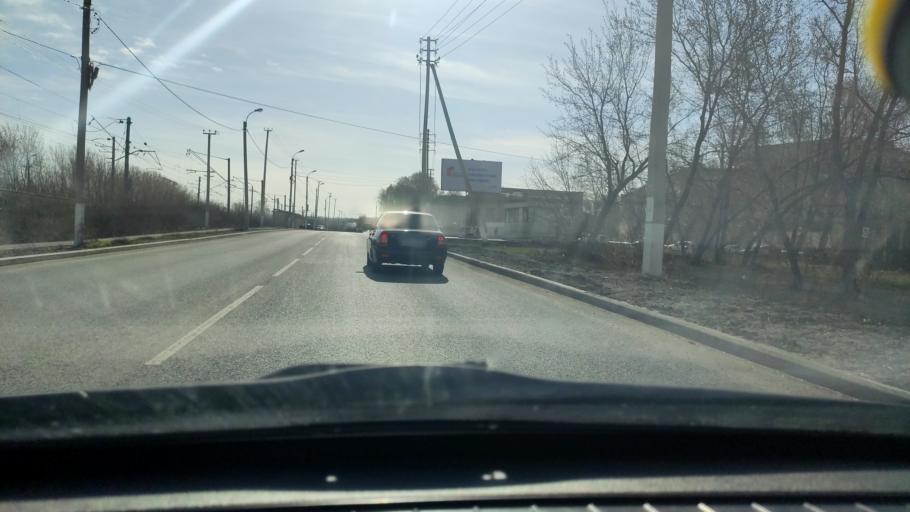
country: RU
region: Samara
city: Zhigulevsk
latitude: 53.4066
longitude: 49.4892
